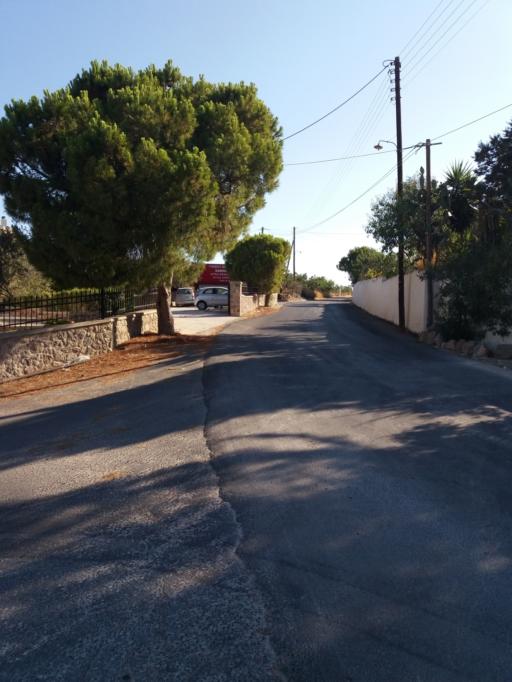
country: GR
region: Attica
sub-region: Nomos Piraios
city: Kypseli
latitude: 37.7427
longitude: 23.4515
